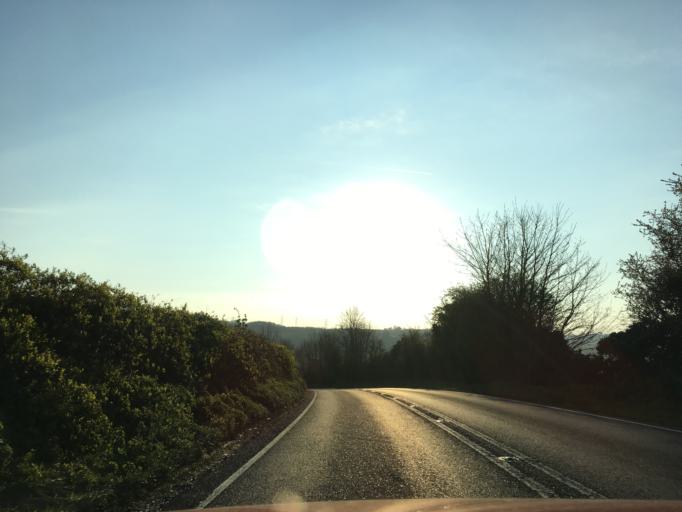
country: GB
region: England
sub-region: Gloucestershire
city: Charlton Kings
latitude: 51.8475
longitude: -2.0596
